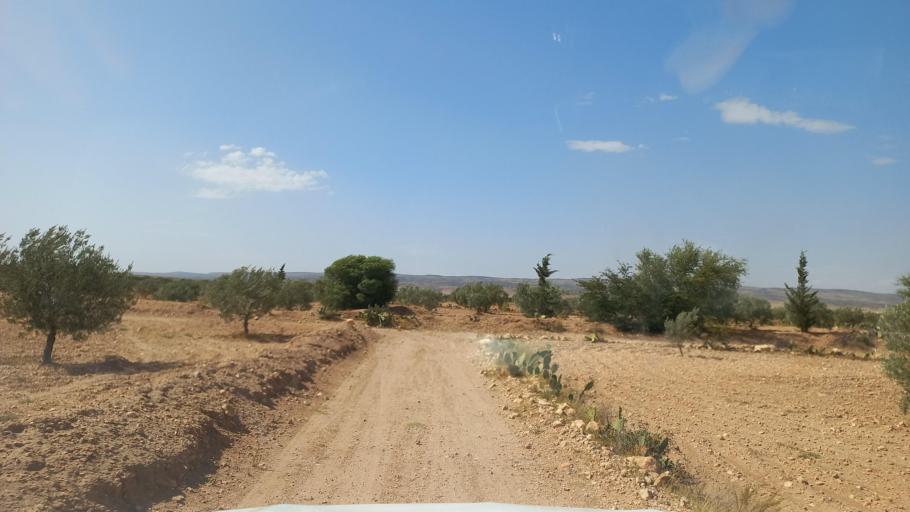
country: TN
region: Al Qasrayn
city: Kasserine
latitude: 35.2586
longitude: 8.9514
